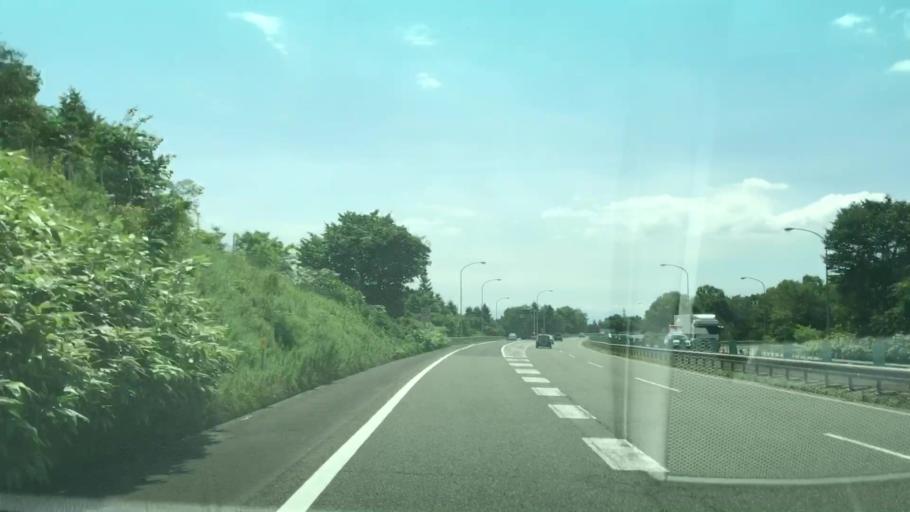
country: JP
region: Hokkaido
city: Muroran
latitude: 42.4024
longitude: 141.0816
